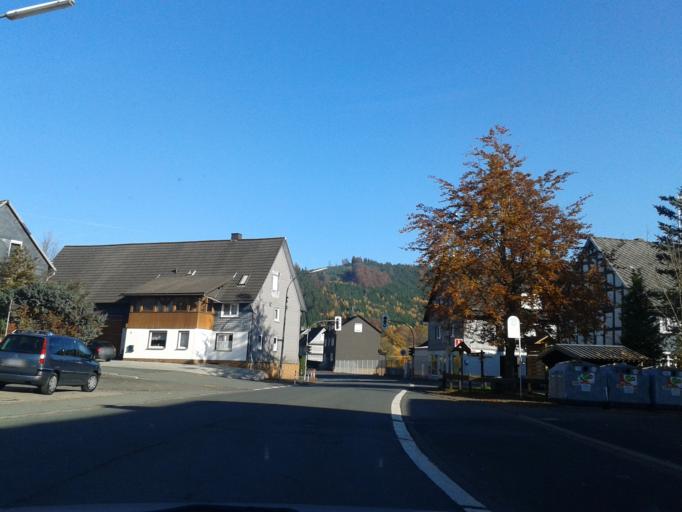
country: DE
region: North Rhine-Westphalia
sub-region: Regierungsbezirk Arnsberg
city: Bad Laasphe
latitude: 50.9147
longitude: 8.3527
